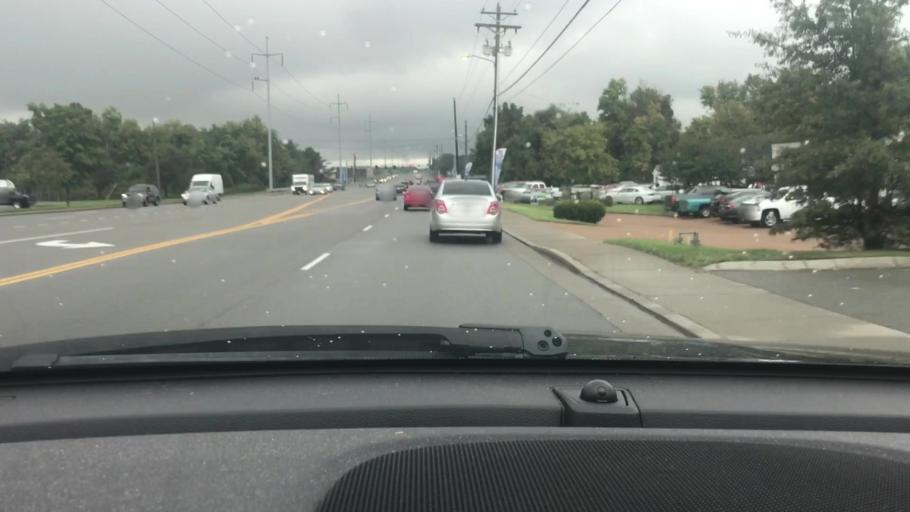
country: US
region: Tennessee
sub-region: Rutherford County
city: La Vergne
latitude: 36.0010
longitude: -86.5960
